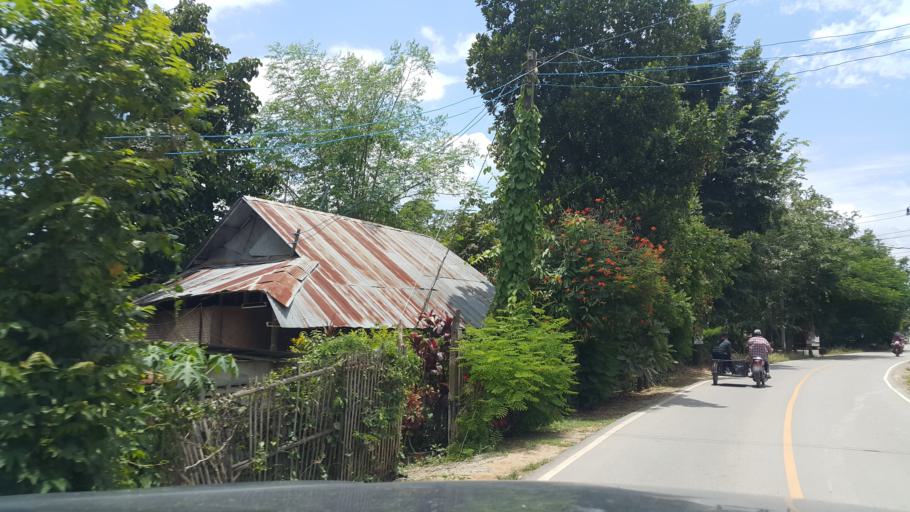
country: TH
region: Chiang Mai
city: Saraphi
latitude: 18.7259
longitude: 98.9891
